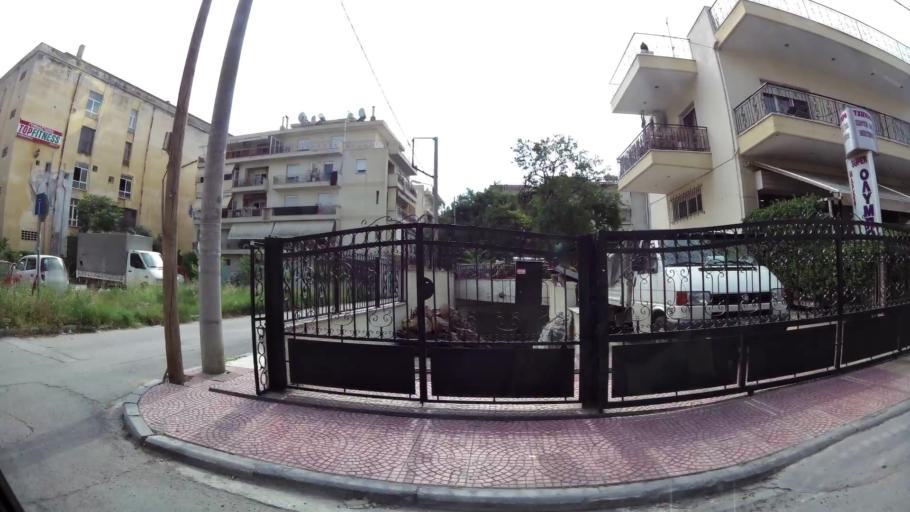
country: GR
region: Central Macedonia
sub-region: Nomos Thessalonikis
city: Stavroupoli
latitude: 40.6787
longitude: 22.9332
